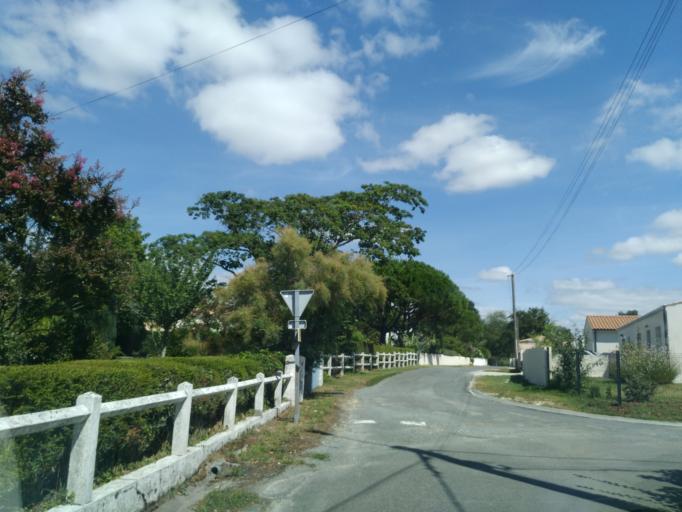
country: FR
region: Poitou-Charentes
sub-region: Departement de la Charente-Maritime
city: Breuillet
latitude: 45.6908
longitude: -1.0733
